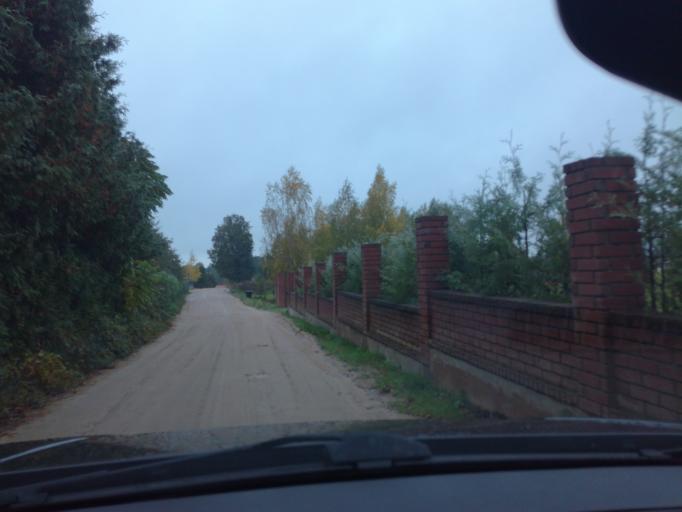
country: LT
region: Alytaus apskritis
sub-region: Alytus
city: Alytus
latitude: 54.3933
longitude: 24.1008
